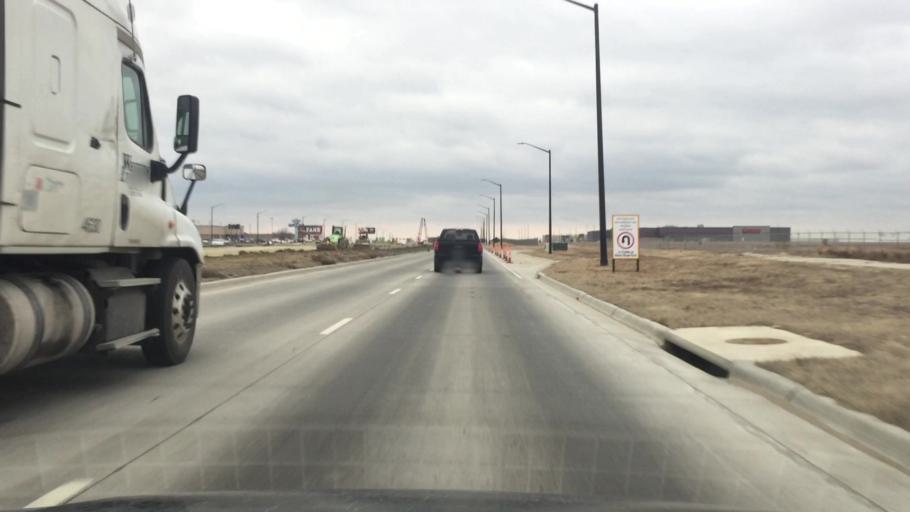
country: US
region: Kansas
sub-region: Butler County
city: Andover
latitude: 37.6794
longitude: -97.2159
